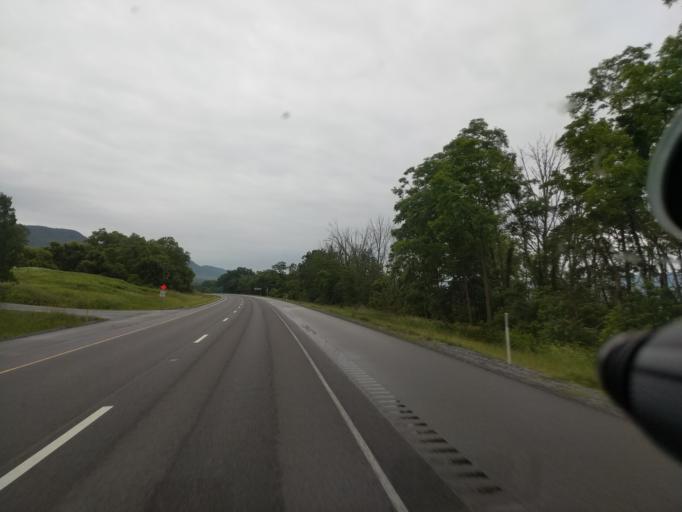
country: US
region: Pennsylvania
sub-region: Clinton County
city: Castanea
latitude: 41.0632
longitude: -77.4281
